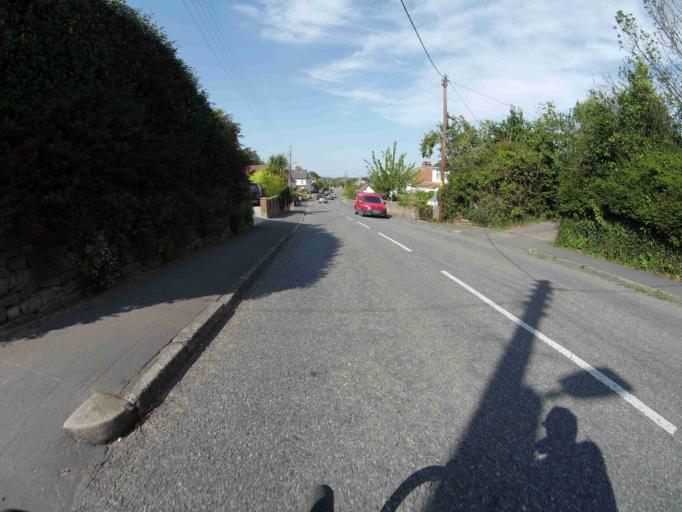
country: GB
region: England
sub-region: Devon
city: Budleigh Salterton
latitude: 50.6358
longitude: -3.3189
